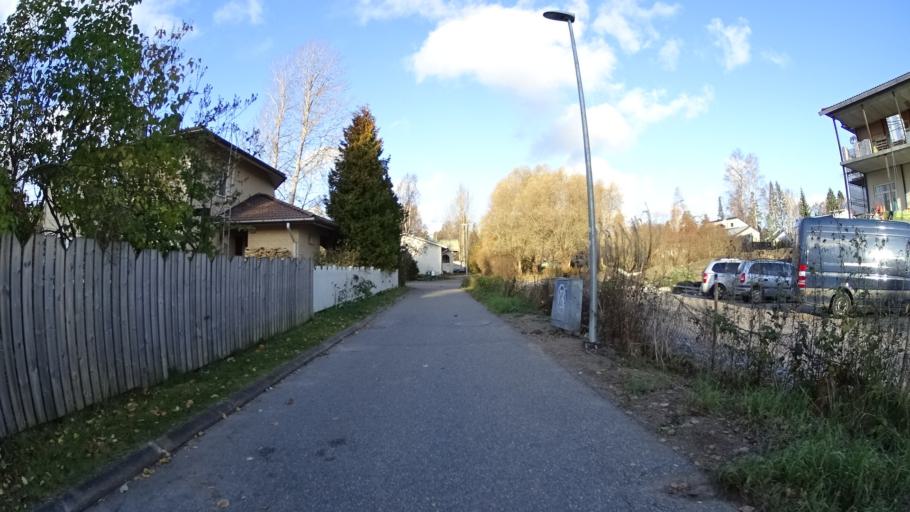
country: FI
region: Uusimaa
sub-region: Helsinki
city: Kilo
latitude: 60.2610
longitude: 24.8260
